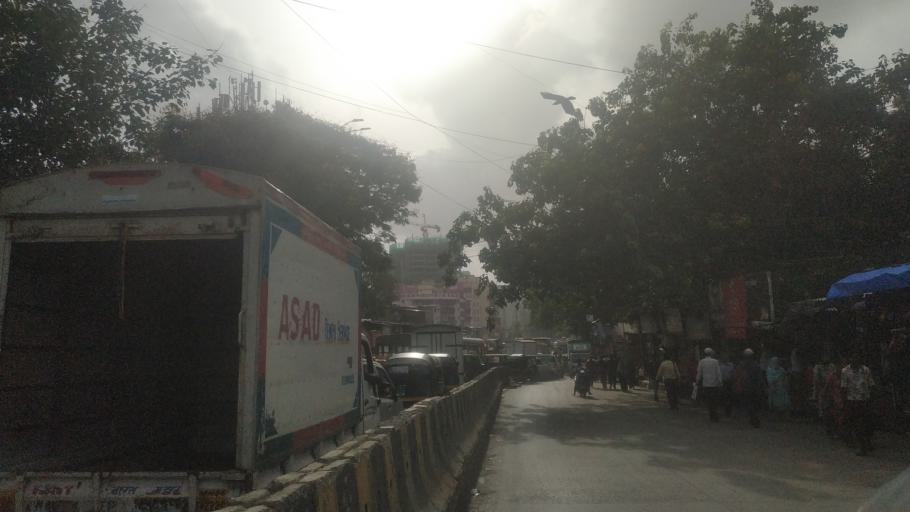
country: IN
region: Maharashtra
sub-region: Mumbai Suburban
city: Mumbai
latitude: 19.0469
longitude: 72.8622
